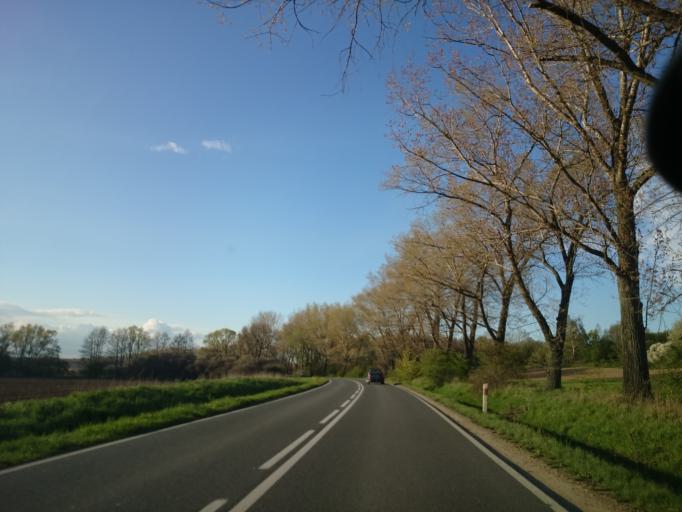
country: PL
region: Lower Silesian Voivodeship
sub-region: Powiat zabkowicki
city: Kamieniec Zabkowicki
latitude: 50.5388
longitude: 16.8646
